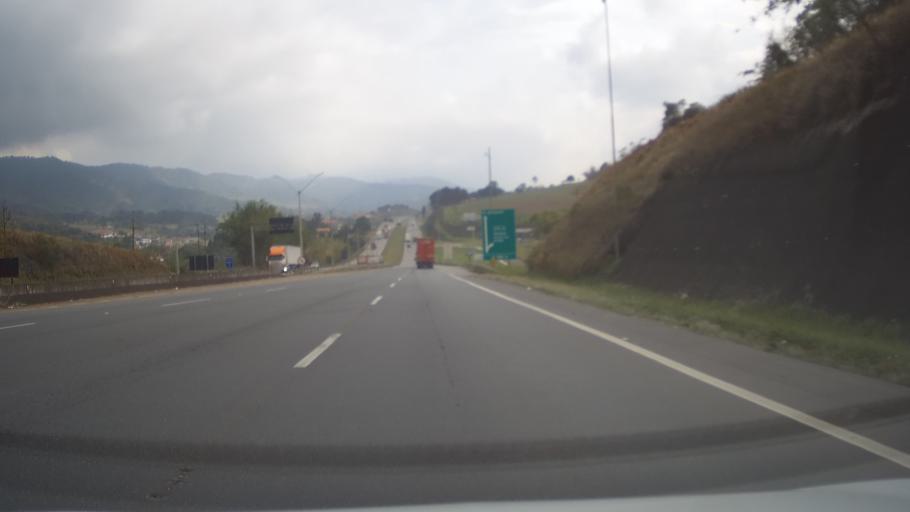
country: BR
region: Minas Gerais
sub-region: Extrema
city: Extrema
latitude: -22.9068
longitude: -46.4232
